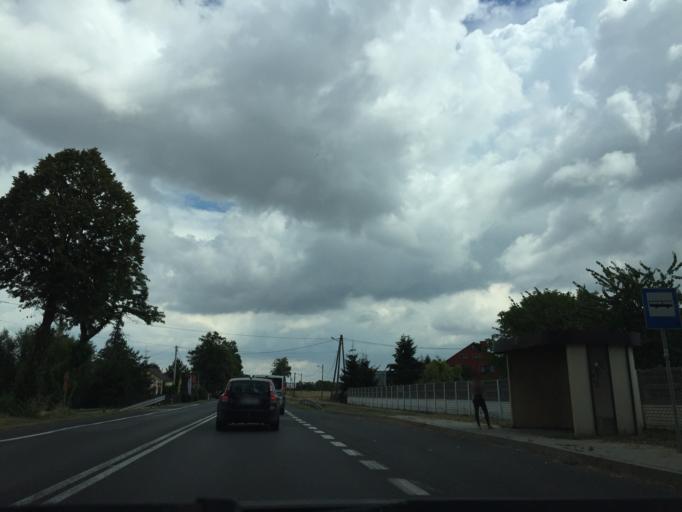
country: PL
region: Lesser Poland Voivodeship
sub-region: Powiat krakowski
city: Slomniki
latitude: 50.2298
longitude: 20.0601
